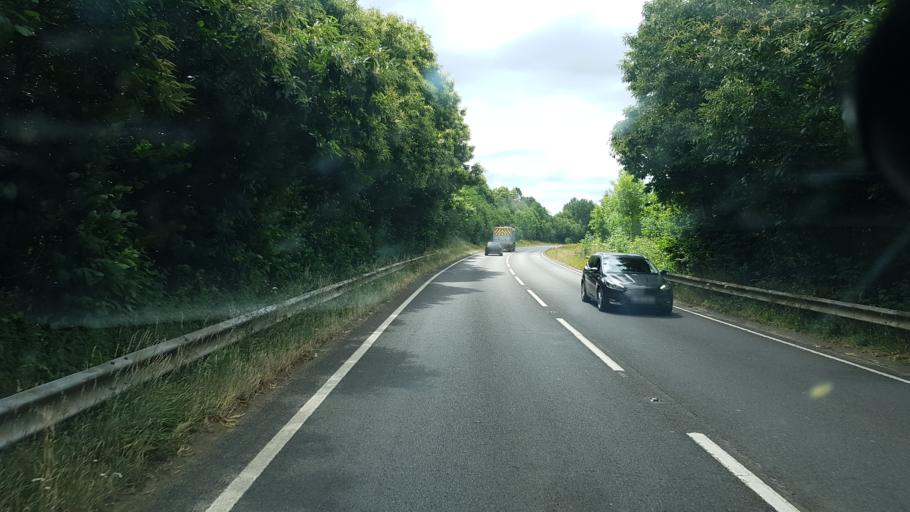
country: GB
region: England
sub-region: Surrey
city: Godstone
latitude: 51.2421
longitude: -0.0474
